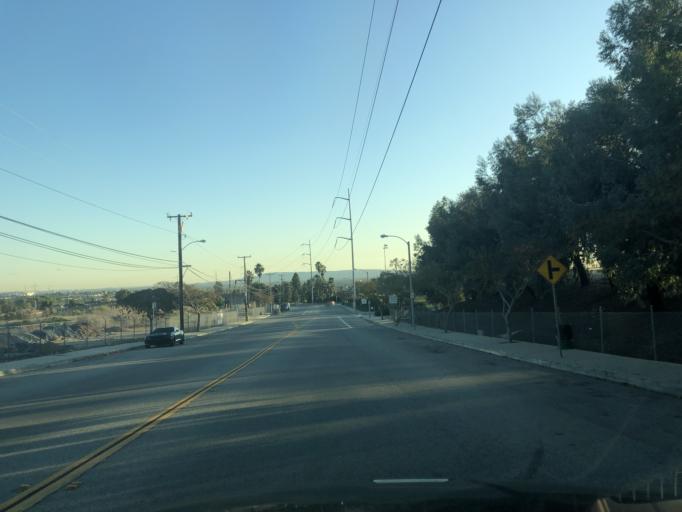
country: US
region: California
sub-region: Los Angeles County
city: Ladera Heights
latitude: 33.9919
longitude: -118.3636
